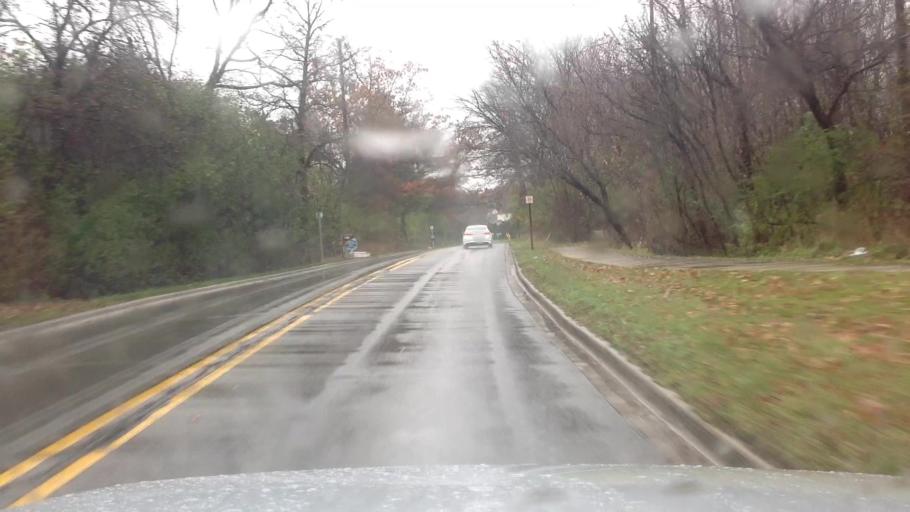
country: US
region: Michigan
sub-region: Oakland County
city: West Bloomfield Township
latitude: 42.5570
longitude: -83.4058
